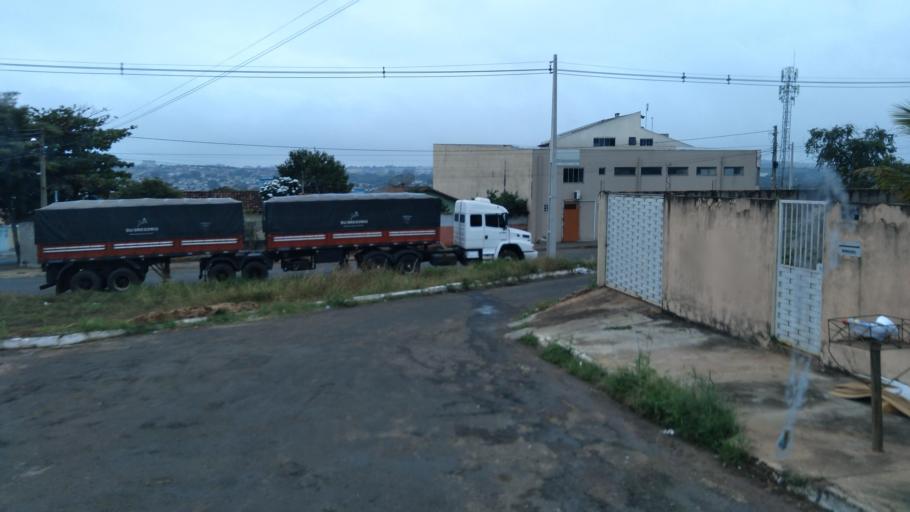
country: BR
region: Goias
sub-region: Mineiros
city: Mineiros
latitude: -17.5719
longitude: -52.5388
